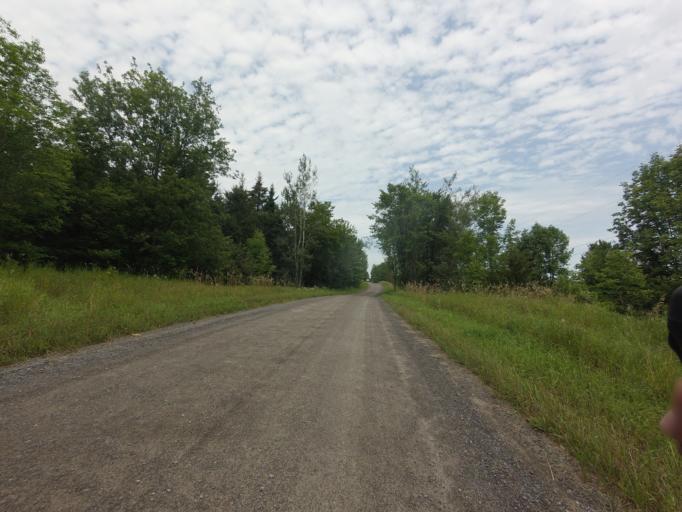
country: CA
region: Ontario
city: Perth
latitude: 44.6839
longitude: -76.6459
